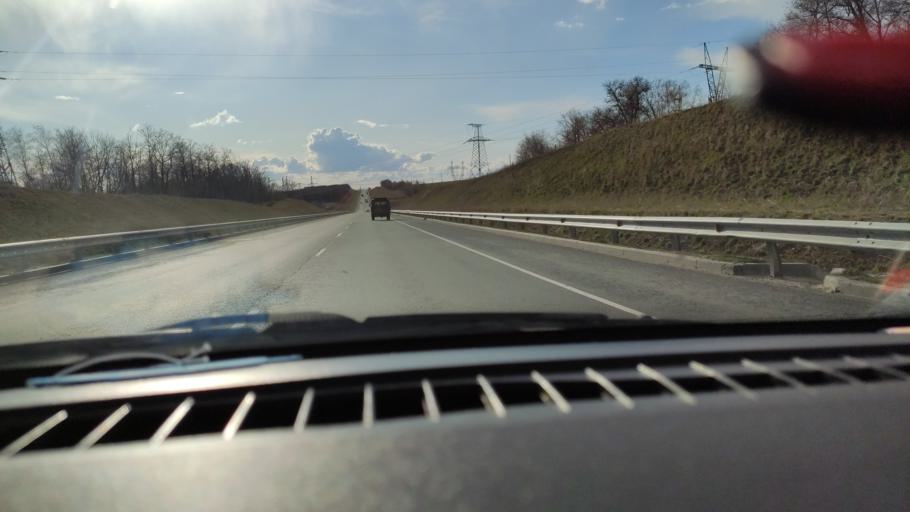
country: RU
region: Saratov
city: Yelshanka
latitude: 51.8231
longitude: 46.3196
